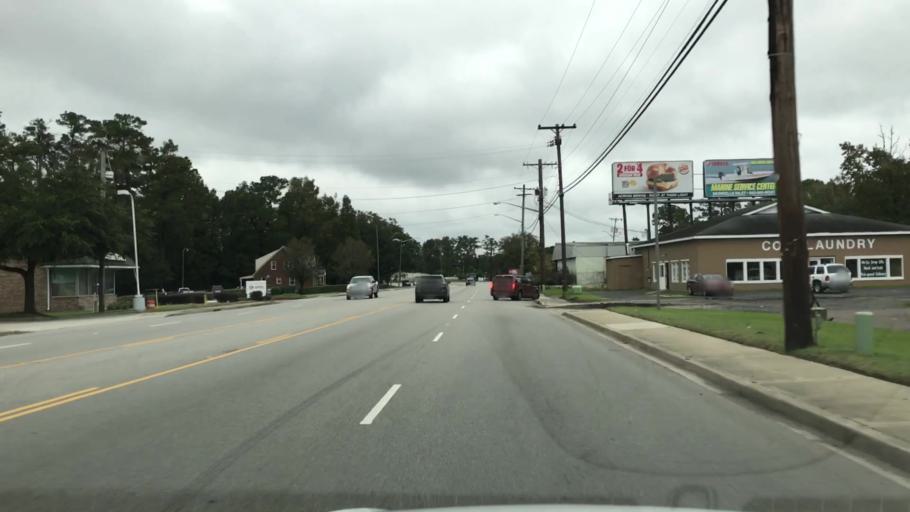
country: US
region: South Carolina
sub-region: Georgetown County
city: Georgetown
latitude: 33.3482
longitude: -79.2947
